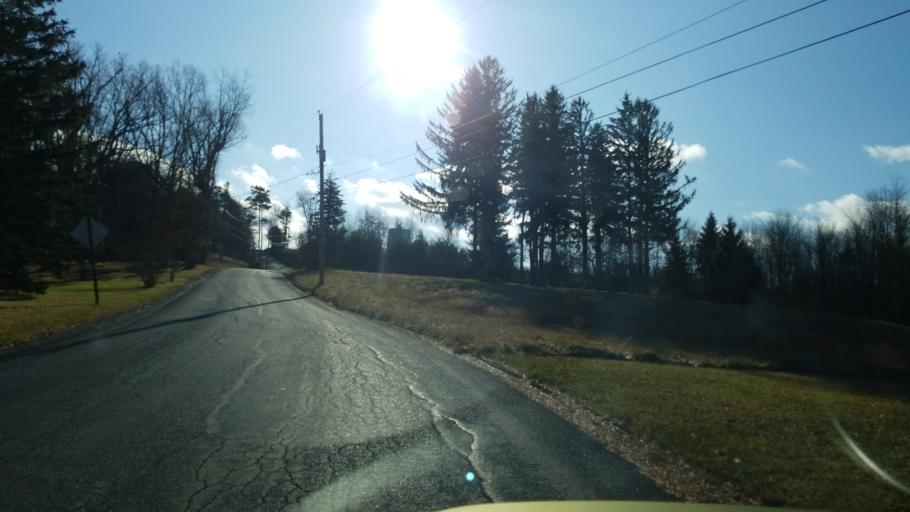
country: US
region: Pennsylvania
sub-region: Clearfield County
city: Clearfield
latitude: 41.0123
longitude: -78.4231
